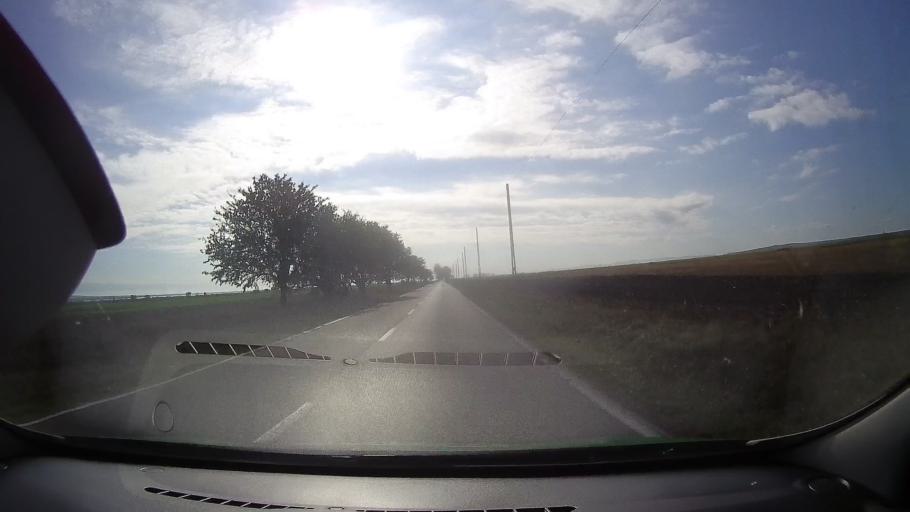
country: RO
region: Tulcea
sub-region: Comuna Valea Nucarilor
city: Agighiol
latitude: 45.0187
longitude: 28.8830
